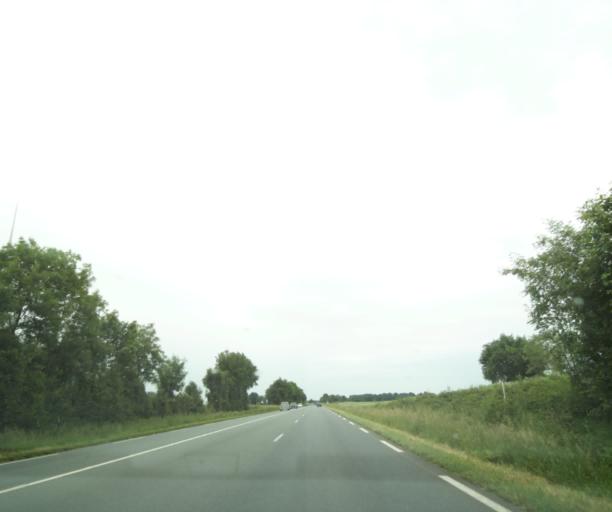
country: FR
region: Poitou-Charentes
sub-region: Departement des Deux-Sevres
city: Champdeniers-Saint-Denis
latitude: 46.4519
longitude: -0.3836
